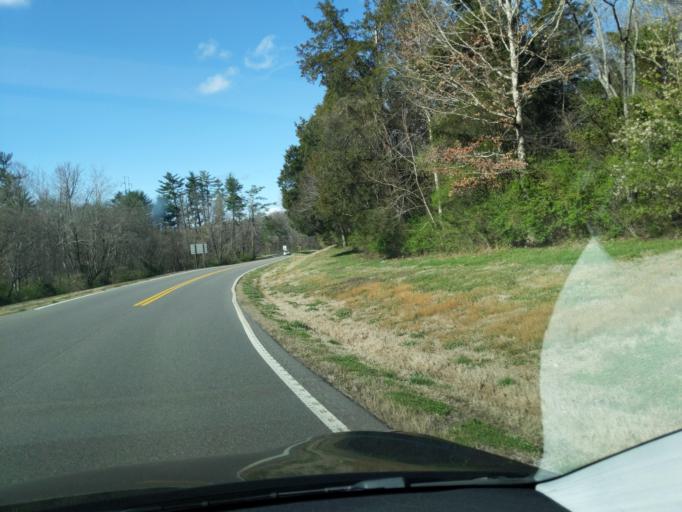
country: US
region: Tennessee
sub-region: Sevier County
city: Sevierville
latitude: 35.9661
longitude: -83.5451
